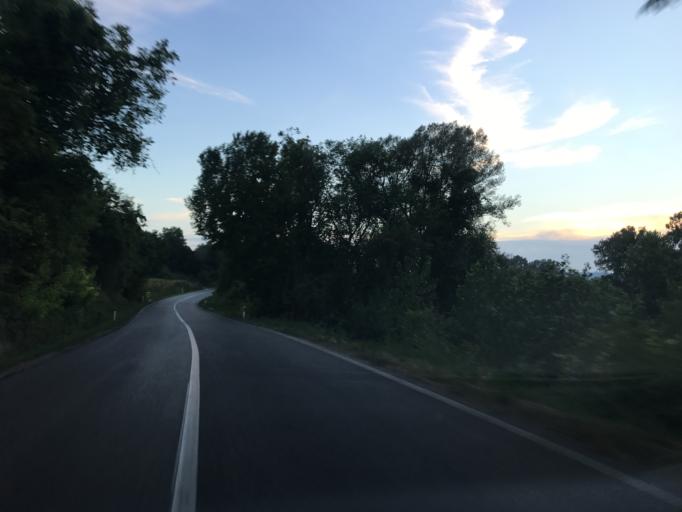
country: RS
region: Central Serbia
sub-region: Branicevski Okrug
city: Veliko Gradiste
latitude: 44.7347
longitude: 21.4751
